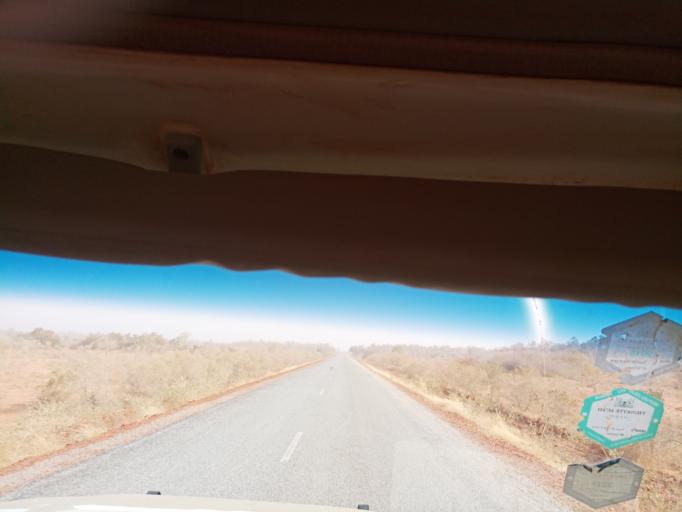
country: NE
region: Tillaberi
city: Say
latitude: 12.8005
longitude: 2.1789
